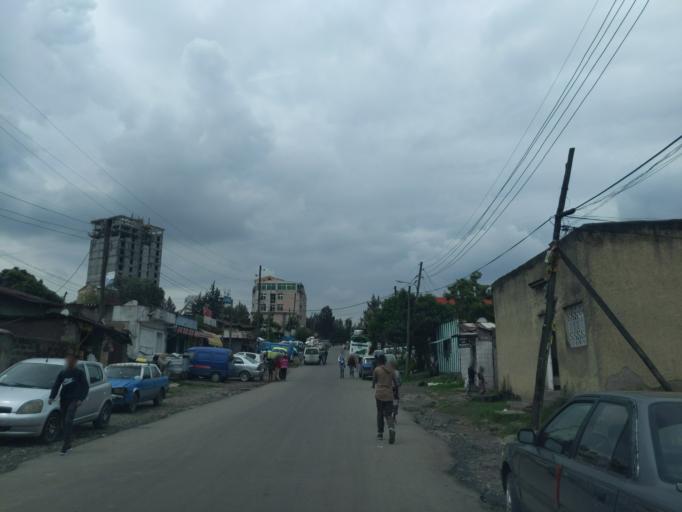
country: ET
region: Adis Abeba
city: Addis Ababa
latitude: 9.0020
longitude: 38.7573
